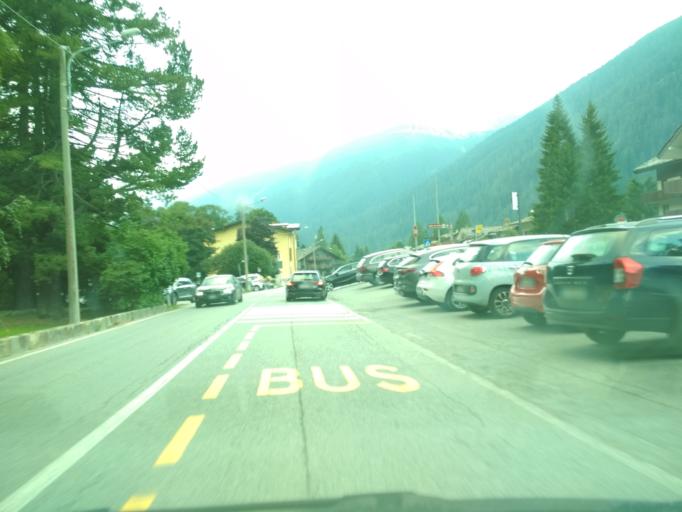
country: IT
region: Aosta Valley
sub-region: Valle d'Aosta
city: Gressoney-Saint-Jean
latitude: 45.7767
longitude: 7.8269
